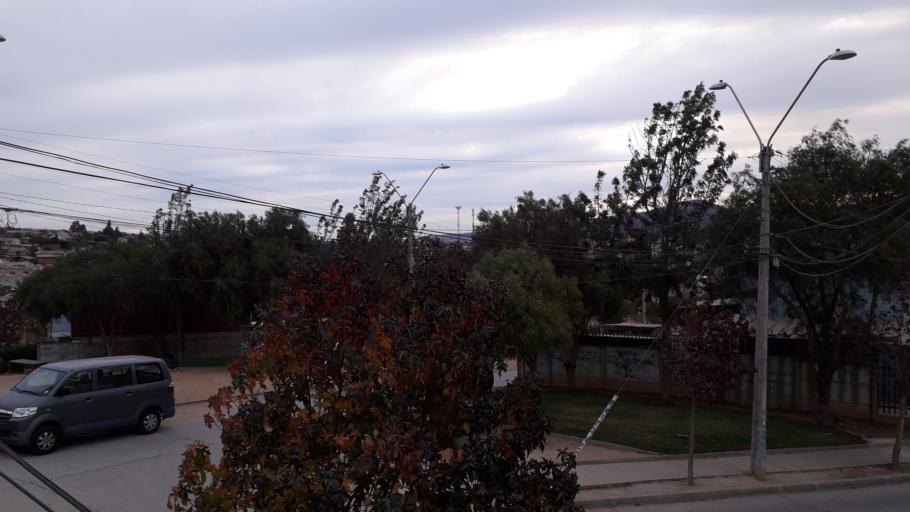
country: CL
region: Valparaiso
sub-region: Provincia de Marga Marga
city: Quilpue
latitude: -33.0519
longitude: -71.4187
